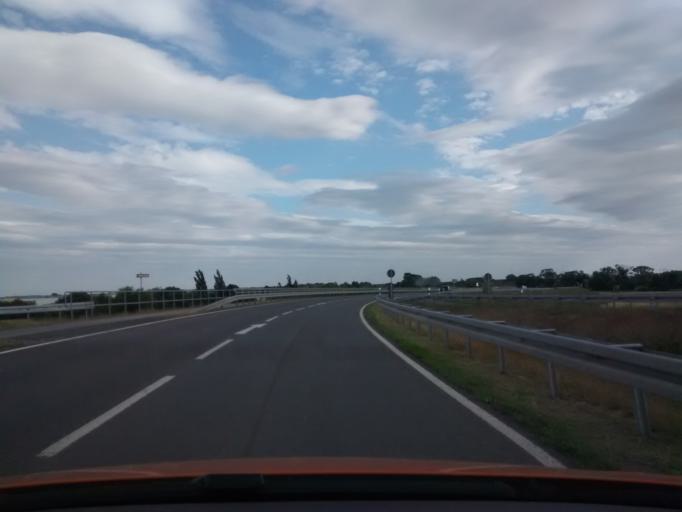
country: DE
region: Berlin
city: Bohnsdorf
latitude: 52.3744
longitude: 13.5505
